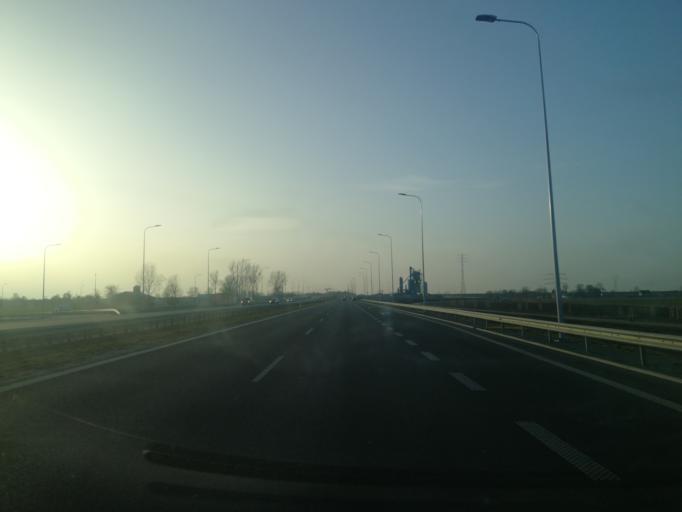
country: PL
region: Pomeranian Voivodeship
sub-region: Powiat nowodworski
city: Ostaszewo
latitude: 54.2550
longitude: 18.9641
